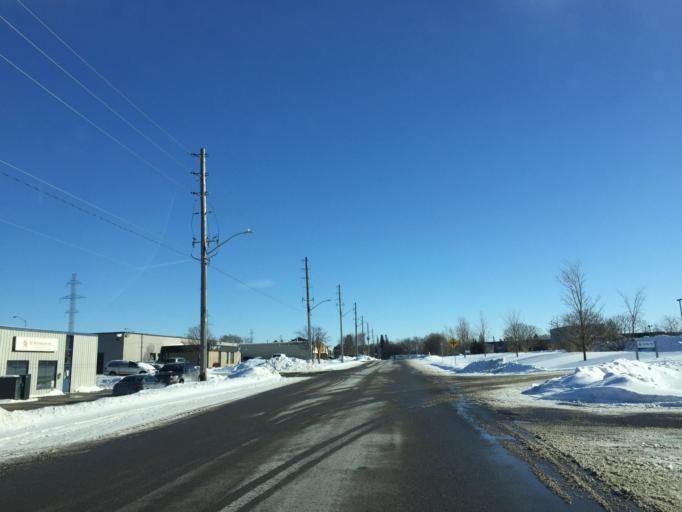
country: CA
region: Ontario
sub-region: Wellington County
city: Guelph
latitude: 43.5454
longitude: -80.2935
